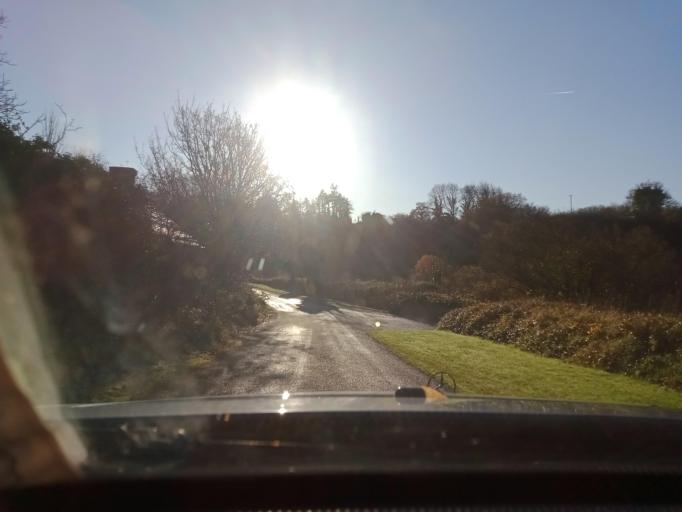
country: IE
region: Munster
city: Carrick-on-Suir
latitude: 52.4269
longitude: -7.3897
